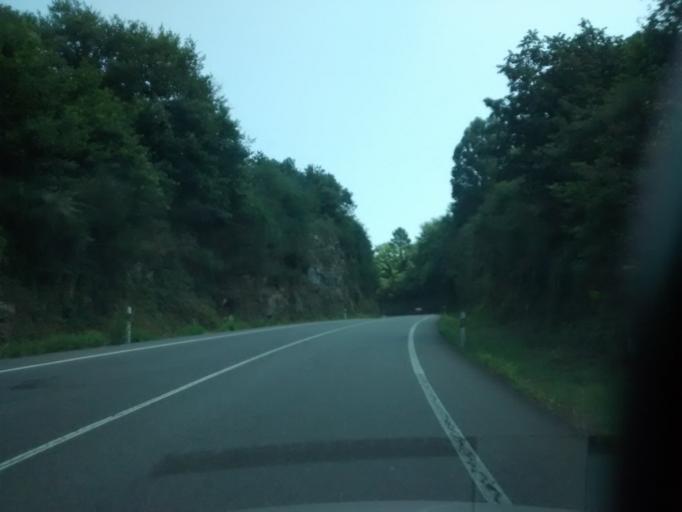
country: ES
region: Galicia
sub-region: Provincia de Ourense
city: O Carballino
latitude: 42.4257
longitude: -8.0996
